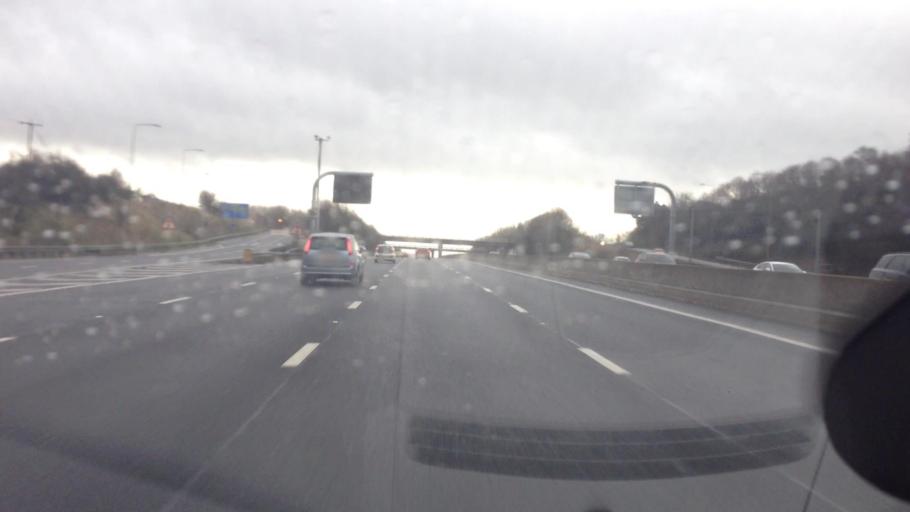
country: GB
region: England
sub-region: City and Borough of Wakefield
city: Ossett
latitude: 53.6869
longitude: -1.5558
